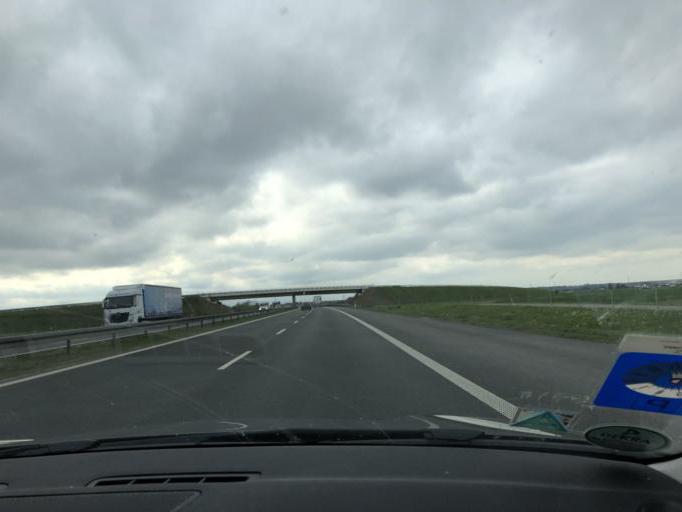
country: PL
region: Opole Voivodeship
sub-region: Powiat krapkowicki
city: Krapkowice
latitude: 50.5230
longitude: 17.9381
